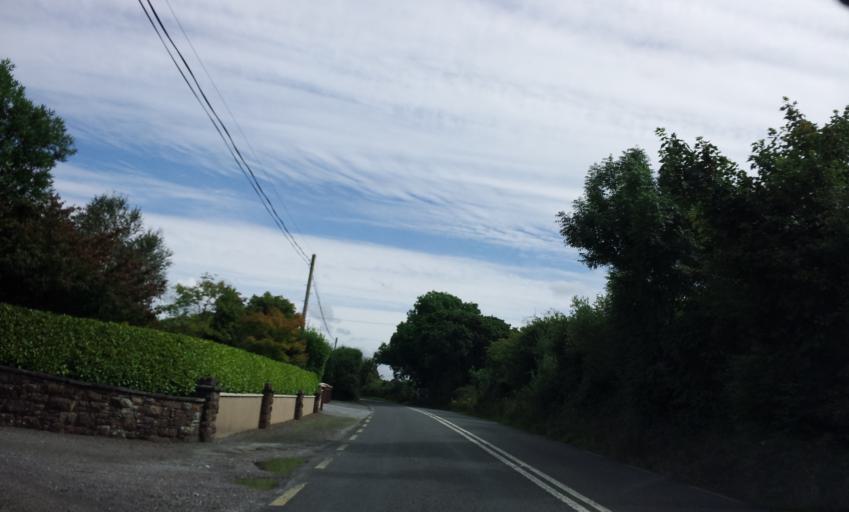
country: IE
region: Munster
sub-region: Ciarrai
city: Killorglin
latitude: 52.0836
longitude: -9.6735
